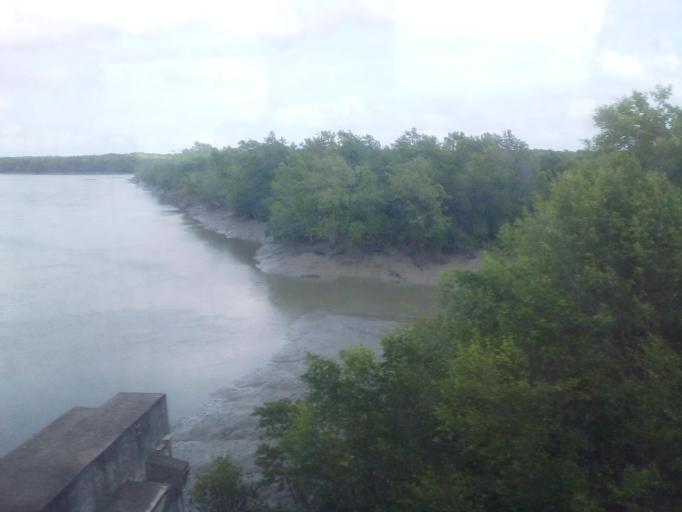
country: BR
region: Maranhao
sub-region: Sao Luis
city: Sao Luis
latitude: -2.7565
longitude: -44.3614
